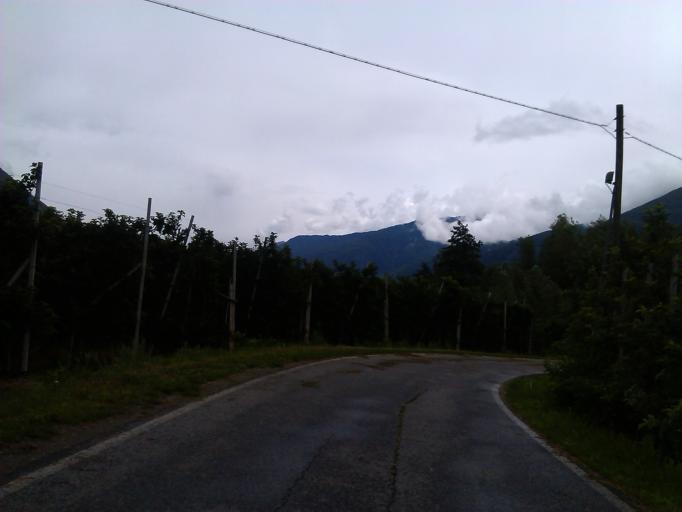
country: IT
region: Trentino-Alto Adige
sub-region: Bolzano
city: Silandro
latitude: 46.6165
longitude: 10.7830
